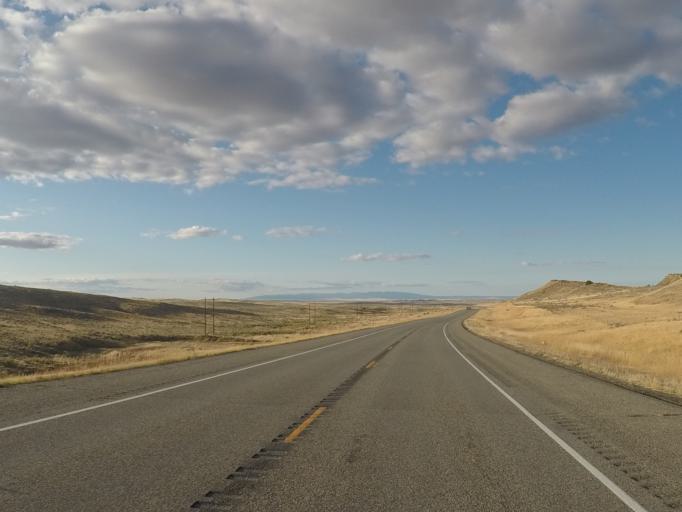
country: US
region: Montana
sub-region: Golden Valley County
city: Ryegate
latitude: 46.1507
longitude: -108.8956
